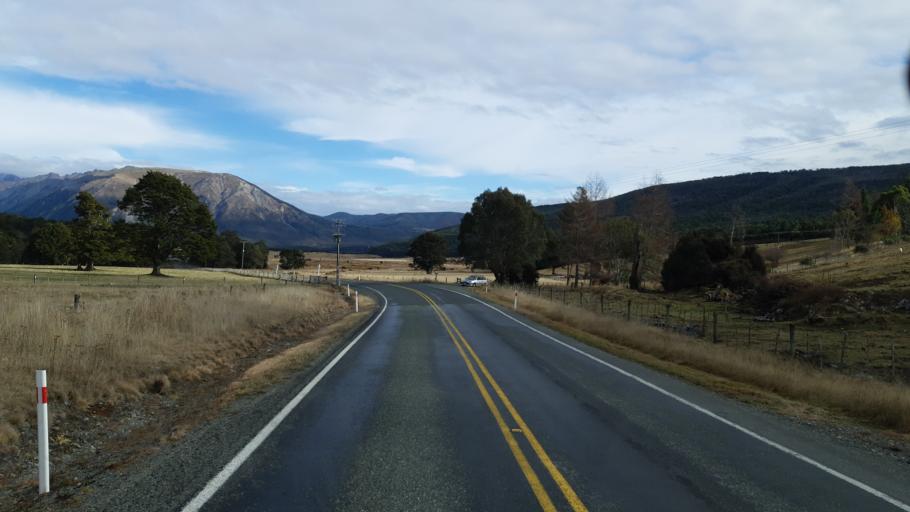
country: NZ
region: Tasman
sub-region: Tasman District
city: Wakefield
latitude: -41.7878
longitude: 172.8867
